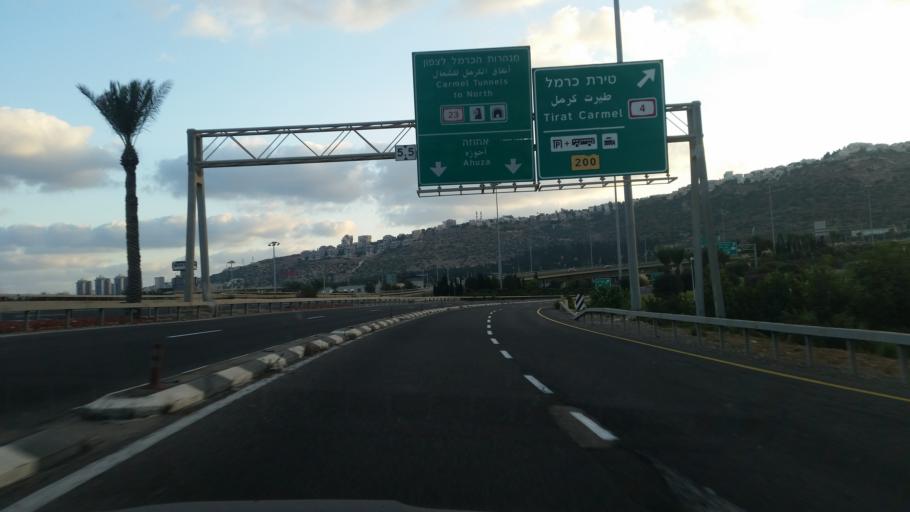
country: IL
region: Haifa
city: Tirat Karmel
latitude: 32.7914
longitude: 34.9578
